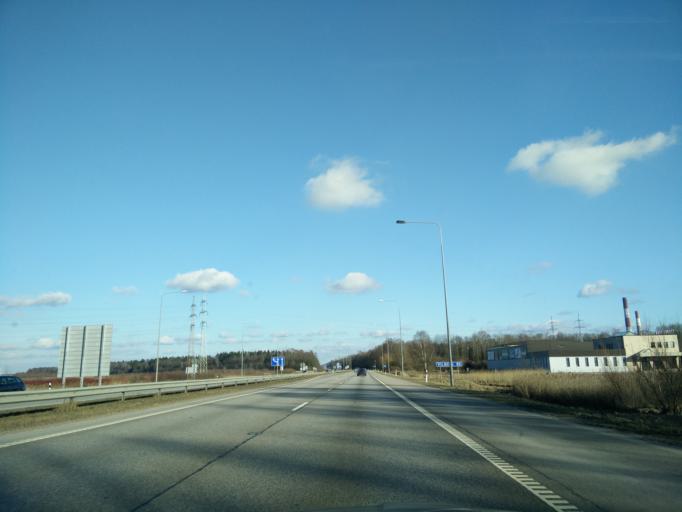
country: LT
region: Kauno apskritis
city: Dainava (Kaunas)
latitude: 54.9314
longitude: 23.9959
